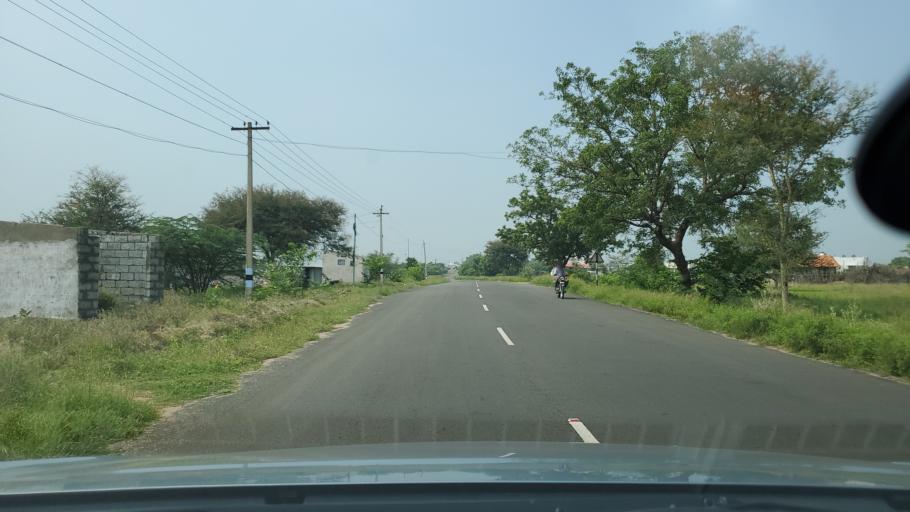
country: IN
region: Tamil Nadu
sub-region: Erode
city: Chennimalai
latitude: 11.2022
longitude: 77.6336
